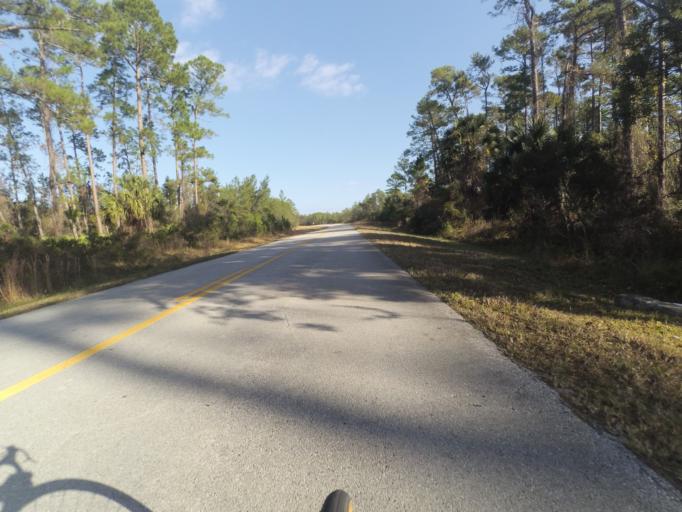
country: US
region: Florida
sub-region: Lake County
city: Astor
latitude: 29.1319
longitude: -81.5769
